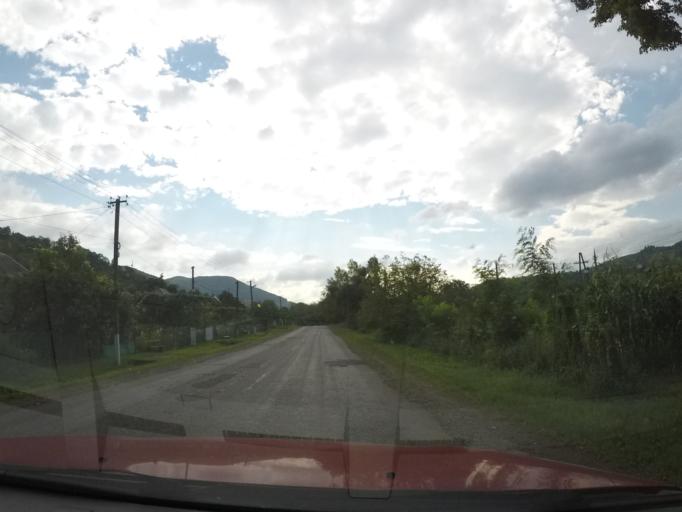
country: UA
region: Zakarpattia
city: Velykyi Bereznyi
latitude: 48.9514
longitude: 22.5385
